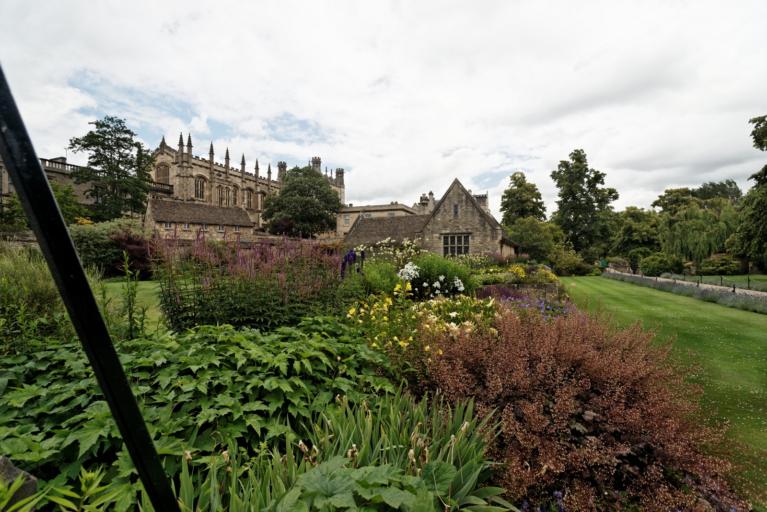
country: GB
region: England
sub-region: Oxfordshire
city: Oxford
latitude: 51.7492
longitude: -1.2566
